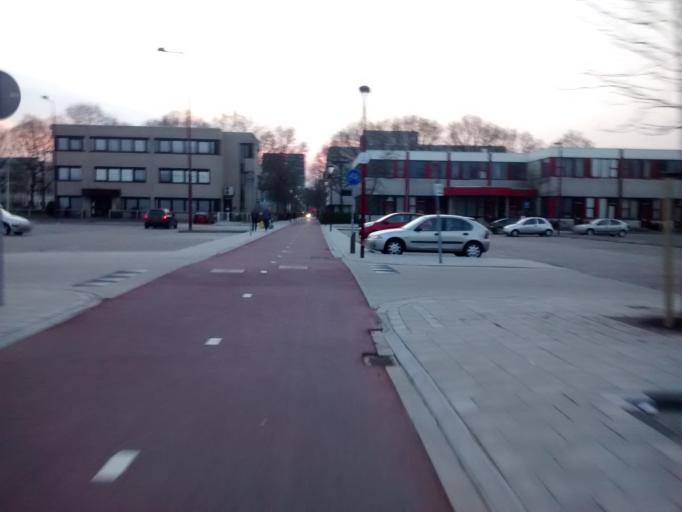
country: NL
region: Utrecht
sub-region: Gemeente Nieuwegein
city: Nieuwegein
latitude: 52.0273
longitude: 5.0932
